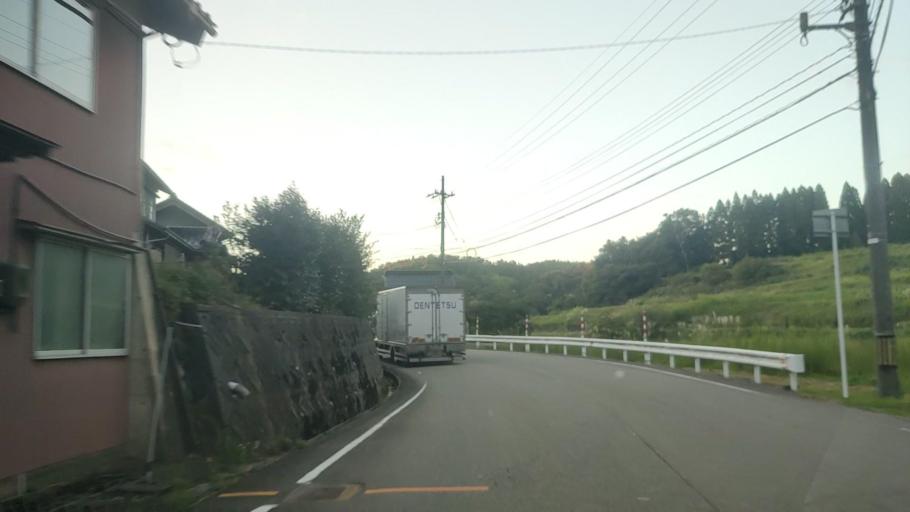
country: JP
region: Ishikawa
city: Tsubata
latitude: 36.6414
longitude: 136.7674
